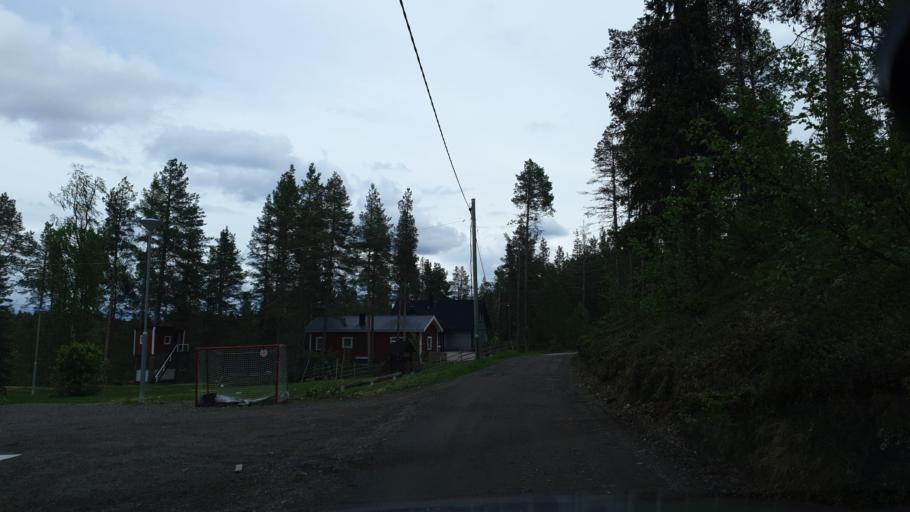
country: SE
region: Norrbotten
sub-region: Kiruna Kommun
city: Kiruna
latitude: 67.8501
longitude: 20.5321
